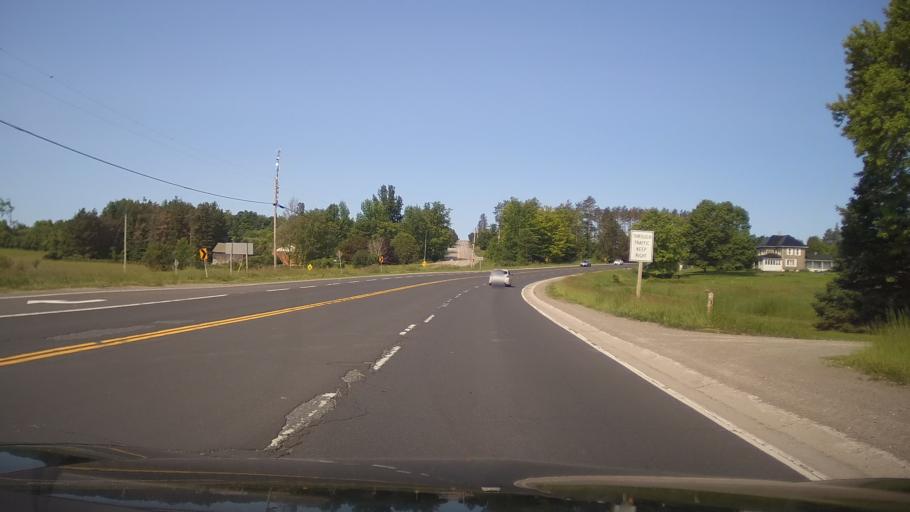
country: CA
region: Ontario
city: Omemee
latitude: 44.2927
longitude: -78.5863
